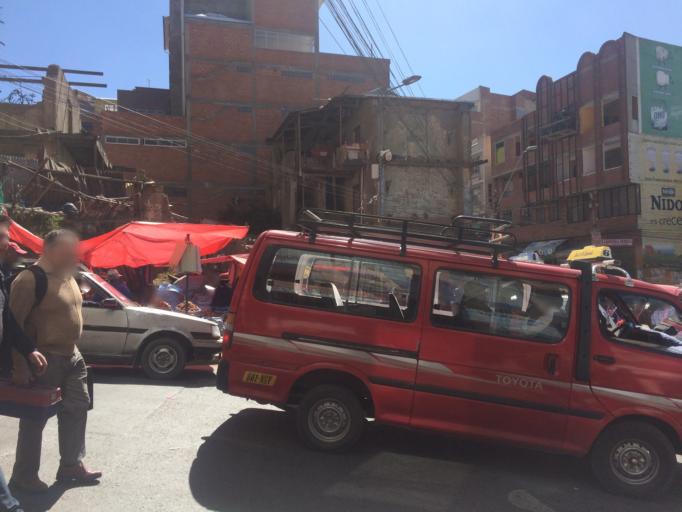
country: BO
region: La Paz
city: La Paz
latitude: -16.5001
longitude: -68.1413
